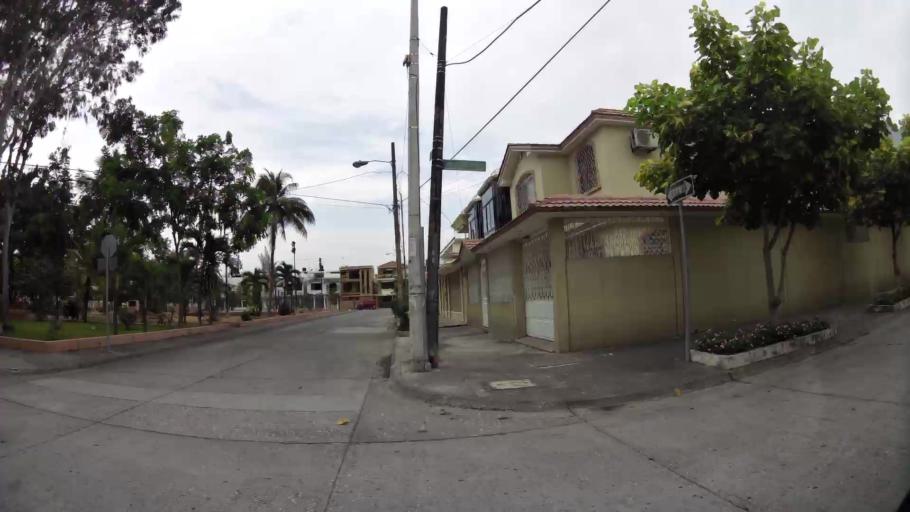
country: EC
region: Guayas
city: Eloy Alfaro
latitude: -2.1440
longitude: -79.8903
